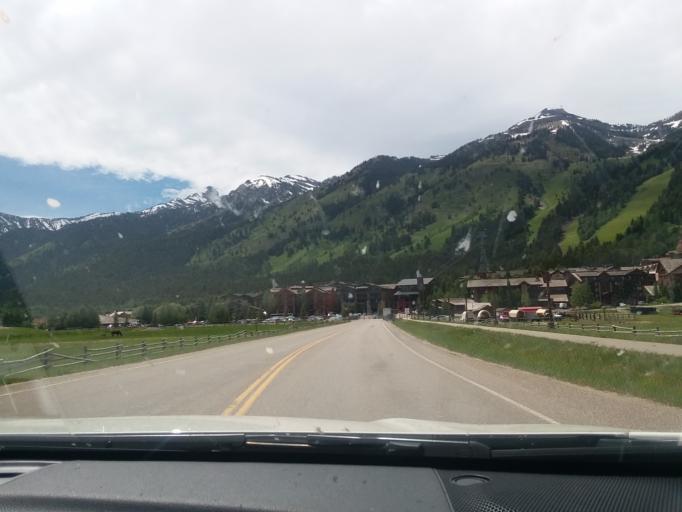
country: US
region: Wyoming
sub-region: Teton County
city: Moose Wilson Road
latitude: 43.5874
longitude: -110.8232
